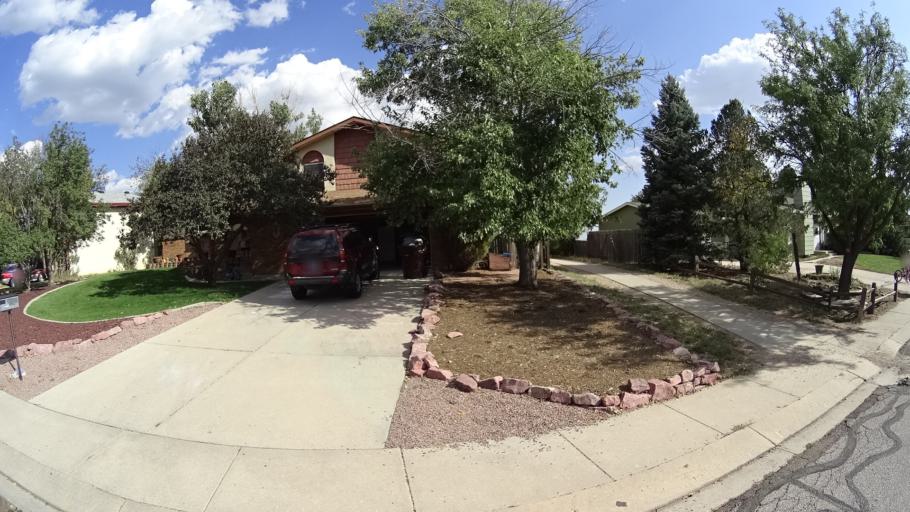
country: US
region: Colorado
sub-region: El Paso County
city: Cimarron Hills
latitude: 38.8724
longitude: -104.7338
